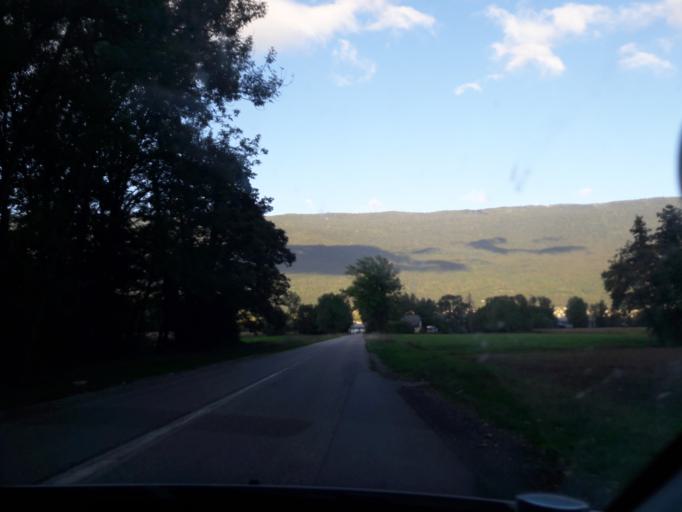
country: FR
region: Rhone-Alpes
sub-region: Departement de la Savoie
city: Voglans
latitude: 45.6379
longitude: 5.8899
